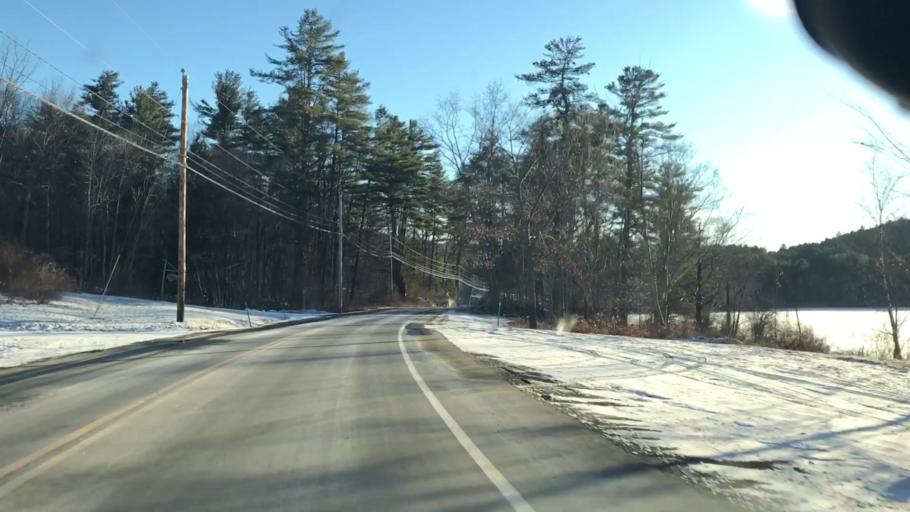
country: US
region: New Hampshire
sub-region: Grafton County
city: Lyme Town Offices
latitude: 43.8293
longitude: -72.1441
